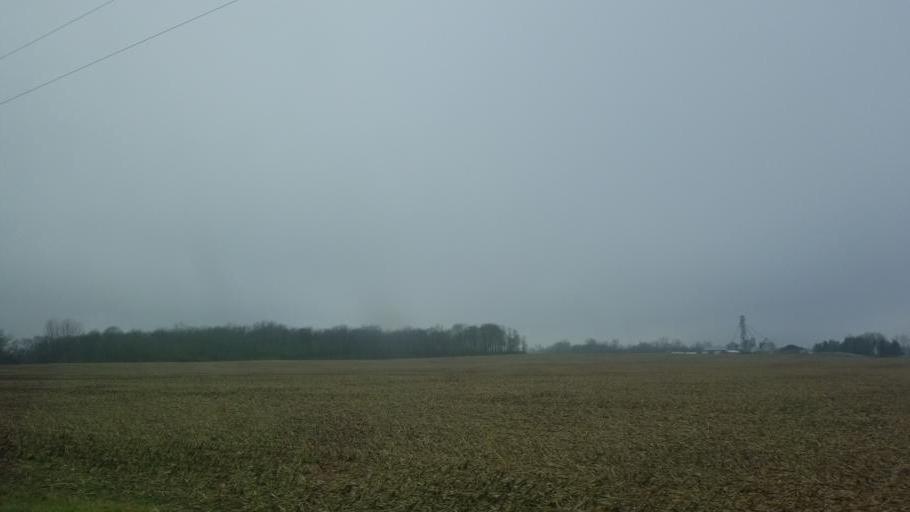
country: US
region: Ohio
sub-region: Champaign County
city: North Lewisburg
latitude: 40.2469
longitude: -83.5374
